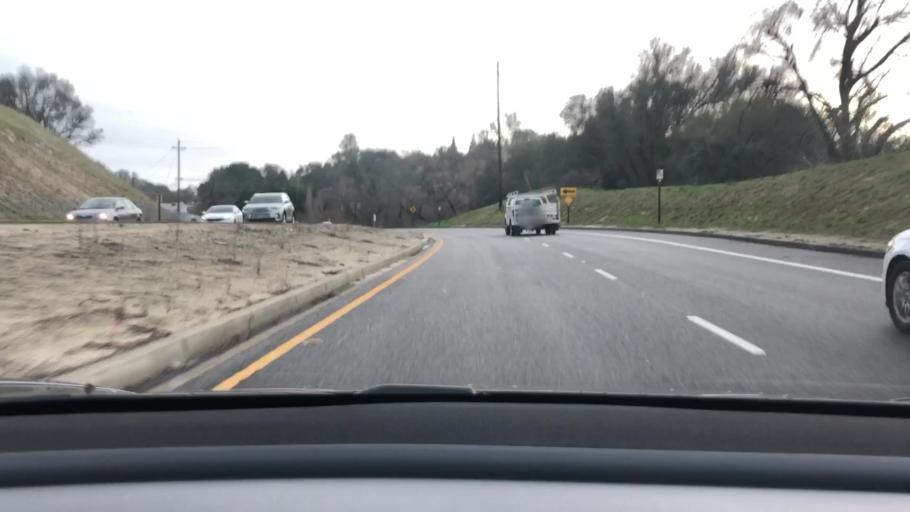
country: US
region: California
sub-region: Placer County
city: Granite Bay
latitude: 38.7267
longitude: -121.1754
